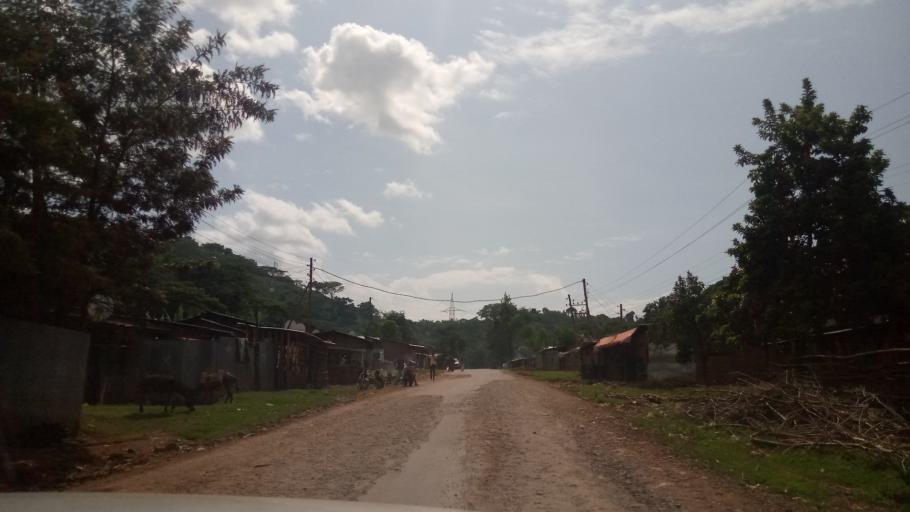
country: ET
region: Oromiya
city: Agaro
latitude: 7.9209
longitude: 36.5197
